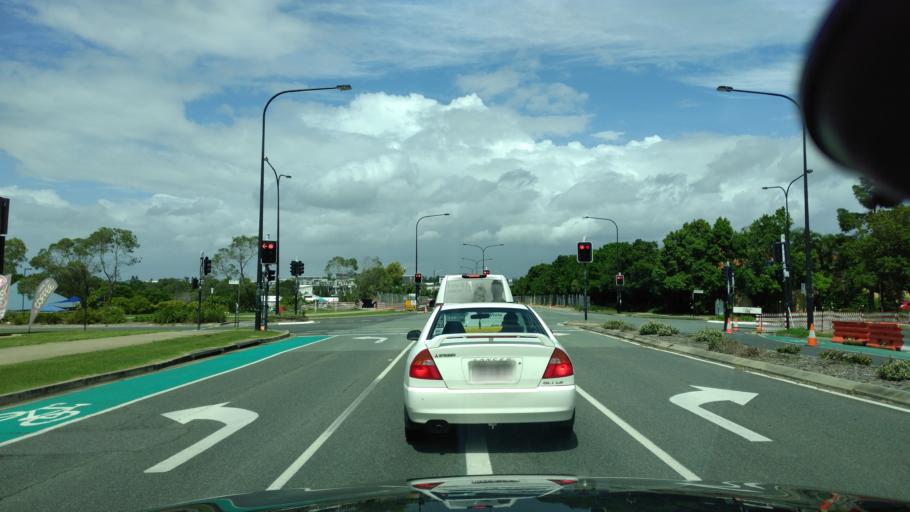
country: AU
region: Queensland
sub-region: Moreton Bay
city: Mango Hill
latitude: -27.2321
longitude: 153.0218
